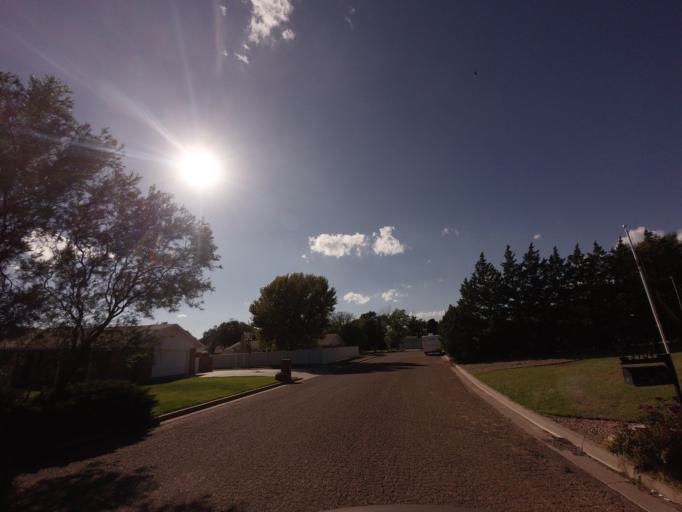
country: US
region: New Mexico
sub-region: Curry County
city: Clovis
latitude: 34.4395
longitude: -103.1802
